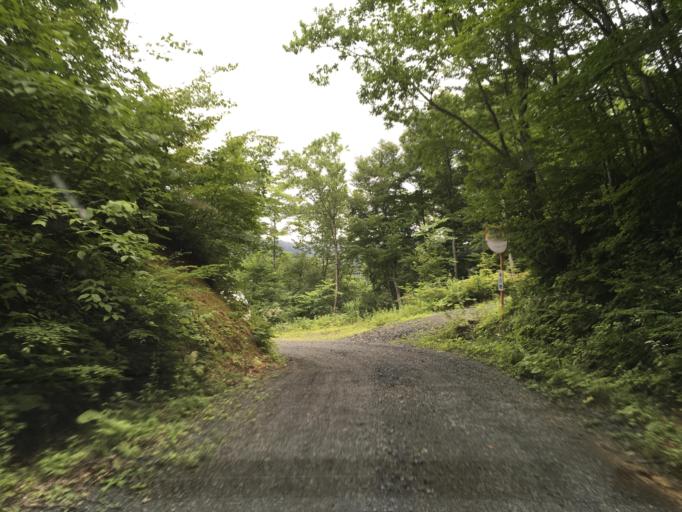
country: JP
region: Iwate
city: Ichinoseki
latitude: 38.9454
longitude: 140.8681
